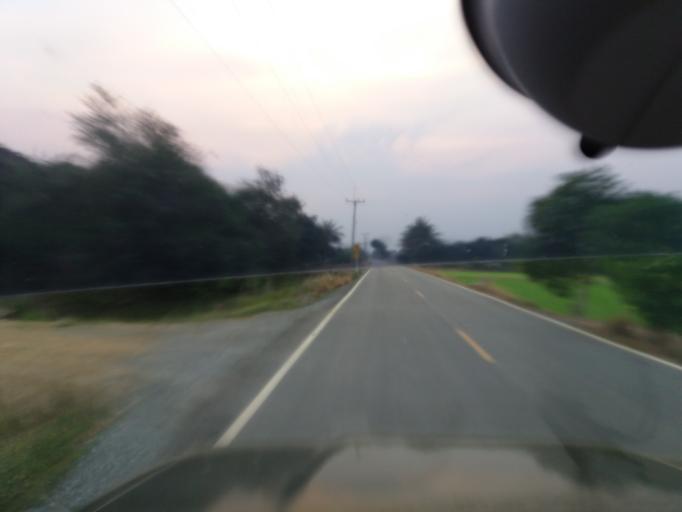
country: TH
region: Suphan Buri
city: Doem Bang Nang Buat
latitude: 14.8912
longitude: 100.1594
